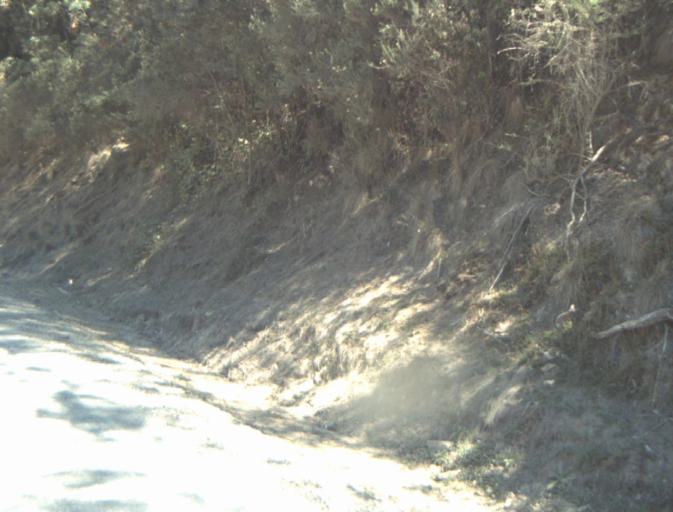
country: AU
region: Tasmania
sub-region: Dorset
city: Scottsdale
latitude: -41.3215
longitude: 147.4147
